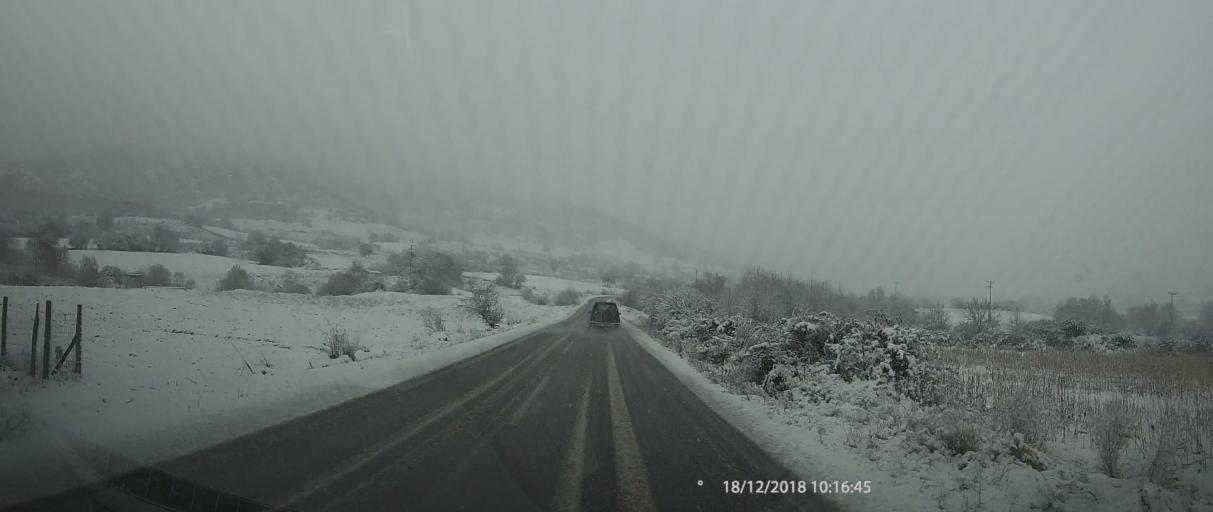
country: GR
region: Thessaly
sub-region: Nomos Larisis
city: Livadi
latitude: 40.1186
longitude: 22.2106
